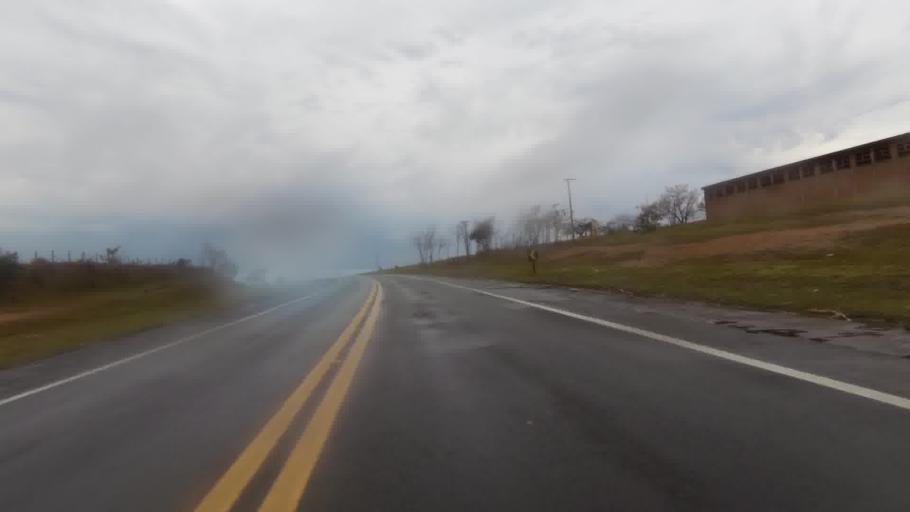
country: BR
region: Rio de Janeiro
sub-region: Campos Dos Goytacazes
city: Campos
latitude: -21.5390
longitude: -41.3423
